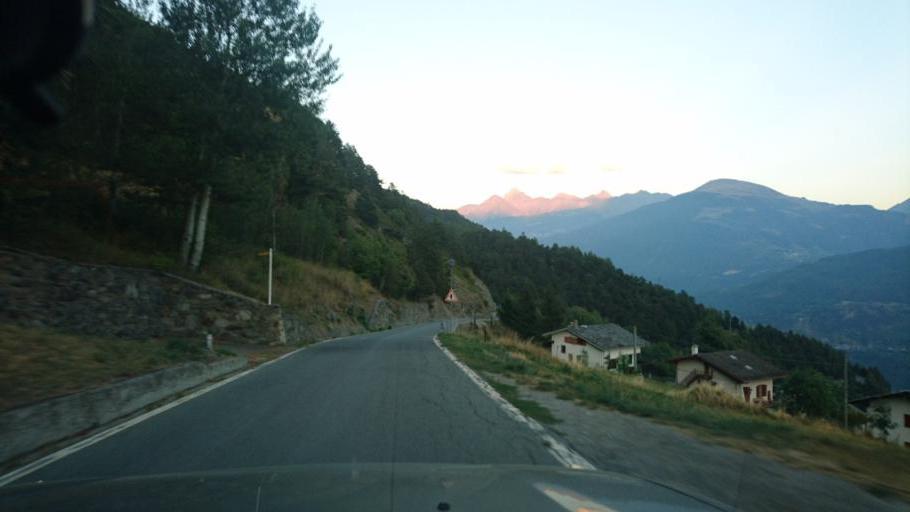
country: IT
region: Aosta Valley
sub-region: Valle d'Aosta
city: Saint-Nicolas
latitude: 45.7175
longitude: 7.1688
